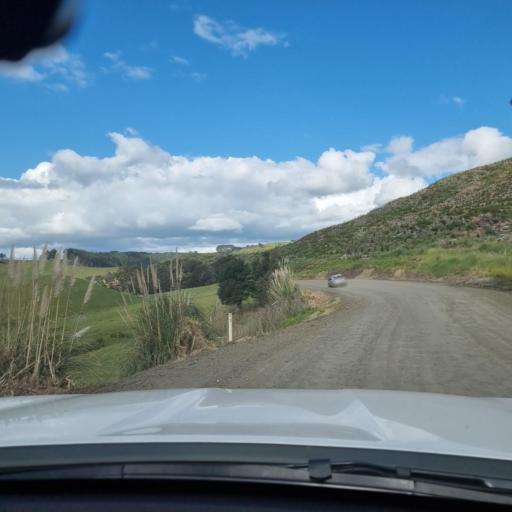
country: NZ
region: Auckland
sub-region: Auckland
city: Wellsford
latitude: -36.3016
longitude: 174.1130
